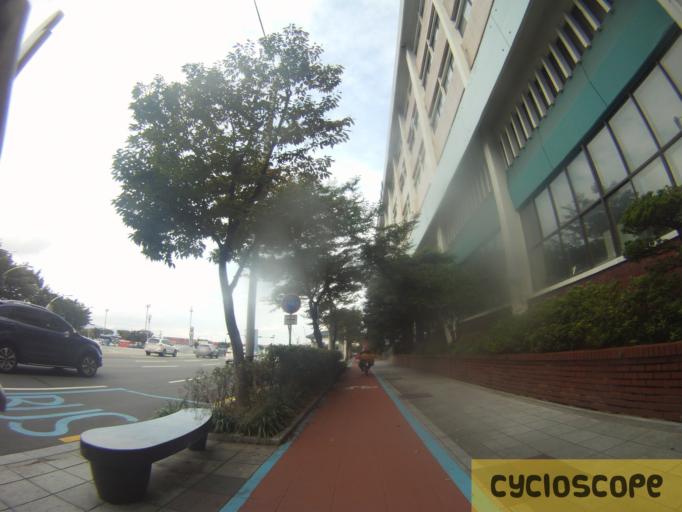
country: KR
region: Busan
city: Busan
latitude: 35.1037
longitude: 129.0408
